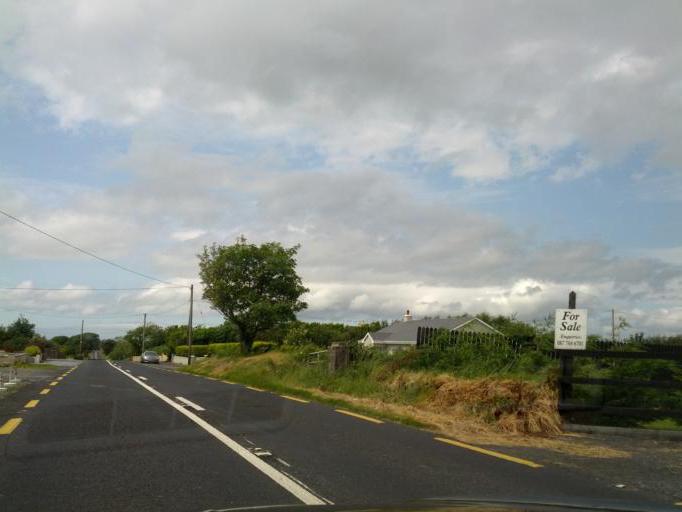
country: IE
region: Munster
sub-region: An Clar
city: Kilrush
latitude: 52.6473
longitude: -9.5010
